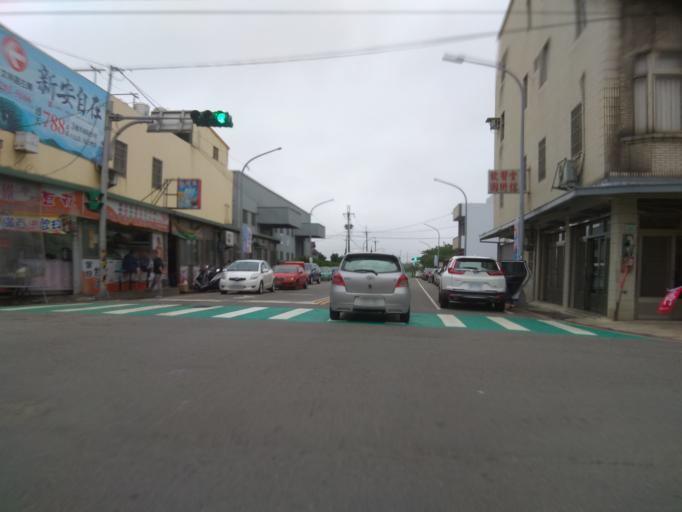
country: TW
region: Taiwan
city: Taoyuan City
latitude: 25.0142
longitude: 121.1336
